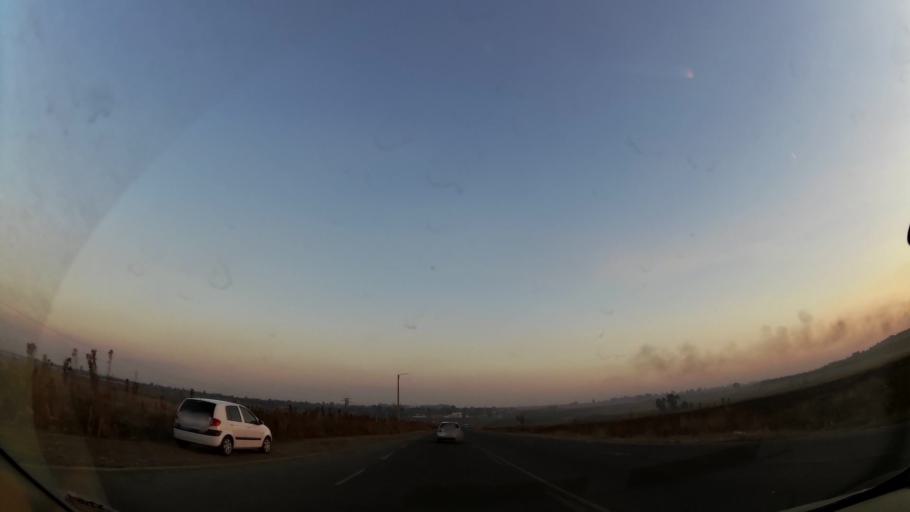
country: ZA
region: Gauteng
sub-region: Ekurhuleni Metropolitan Municipality
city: Springs
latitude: -26.3308
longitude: 28.4232
